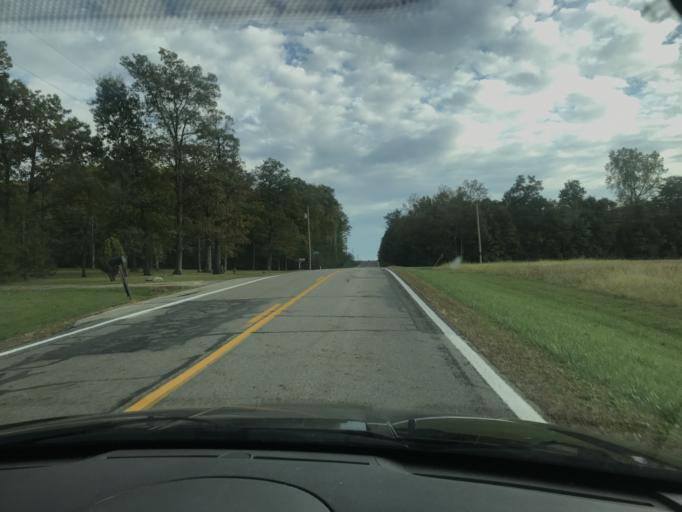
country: US
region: Ohio
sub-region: Champaign County
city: North Lewisburg
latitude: 40.2331
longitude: -83.6439
